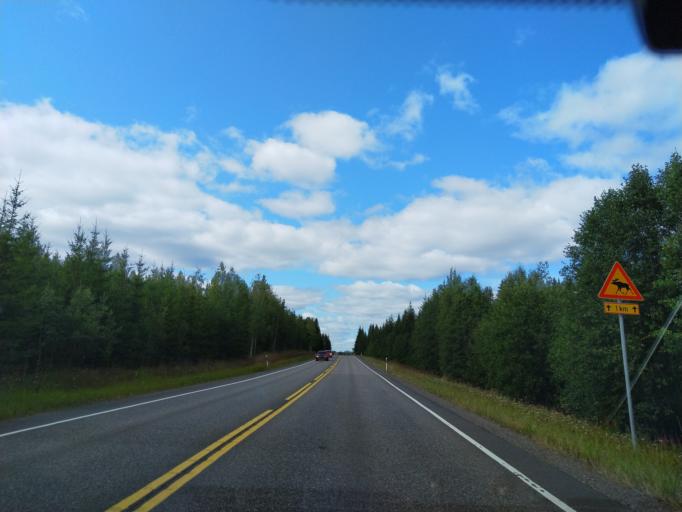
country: FI
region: Haeme
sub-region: Haemeenlinna
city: Renko
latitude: 60.7655
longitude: 24.2564
